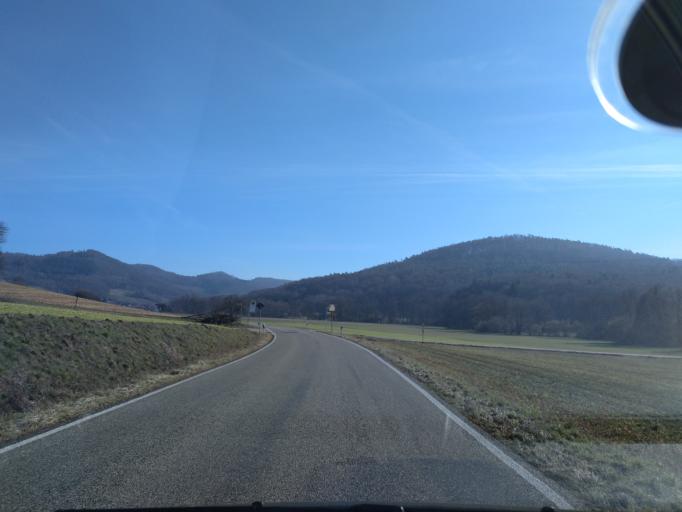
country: DE
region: Baden-Wuerttemberg
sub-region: Regierungsbezirk Stuttgart
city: Pfedelbach
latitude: 49.1475
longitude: 9.4815
